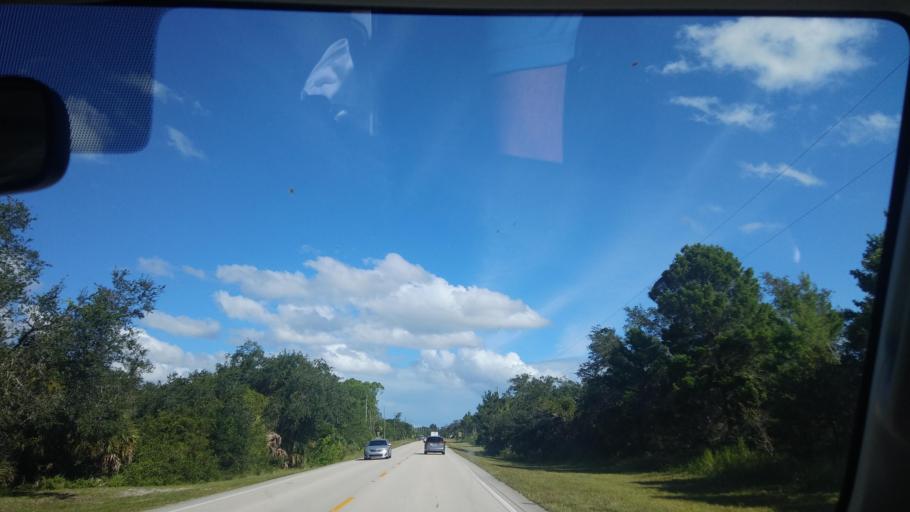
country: US
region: Florida
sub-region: Indian River County
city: Roseland
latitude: 27.8152
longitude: -80.5039
